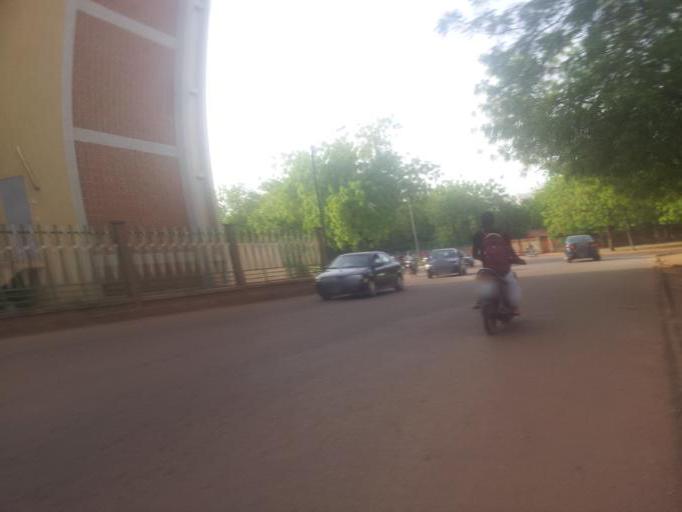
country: BF
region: Centre
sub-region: Kadiogo Province
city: Ouagadougou
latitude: 12.3745
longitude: -1.5089
